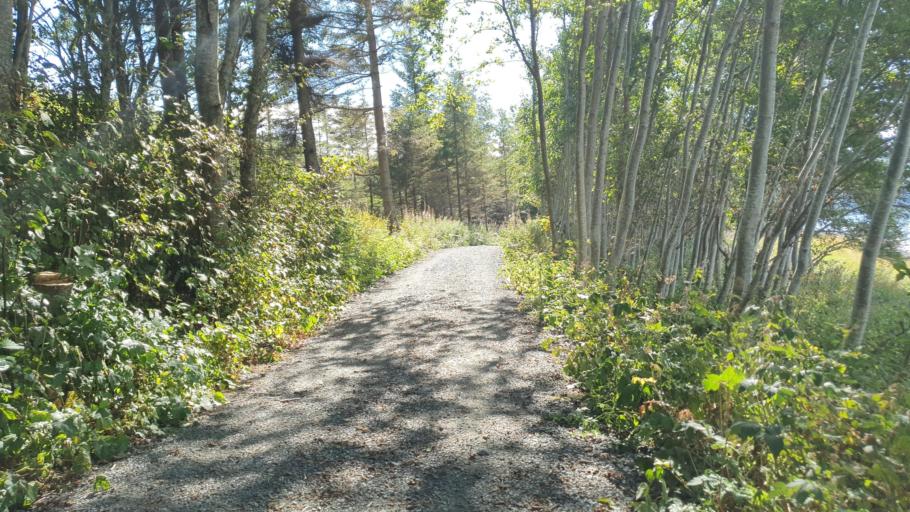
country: NO
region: Nord-Trondelag
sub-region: Levanger
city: Levanger
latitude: 63.7790
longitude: 11.3838
